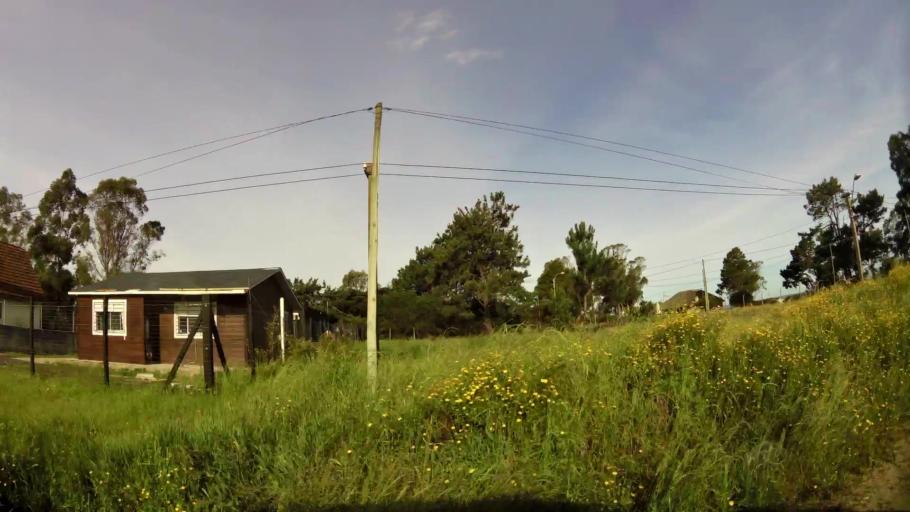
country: UY
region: Canelones
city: Atlantida
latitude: -34.7876
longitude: -55.8487
